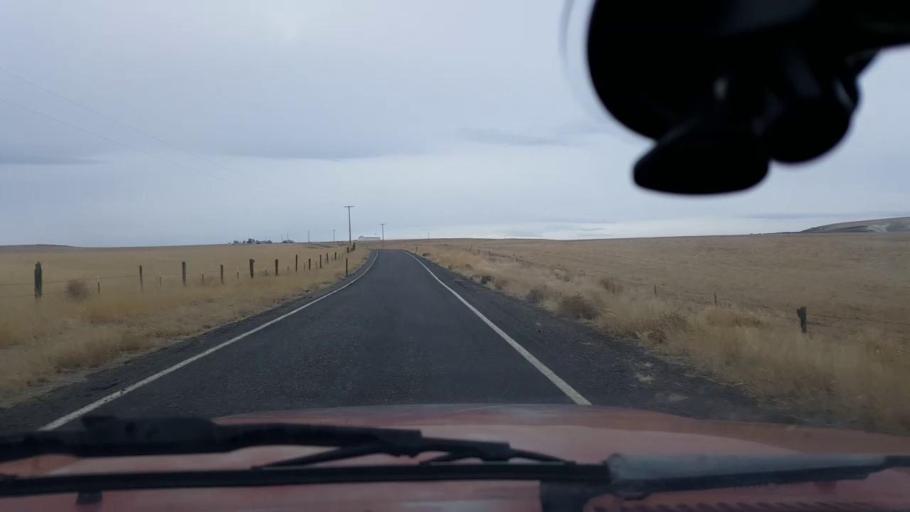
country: US
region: Washington
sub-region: Asotin County
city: Clarkston Heights-Vineland
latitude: 46.3285
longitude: -117.3227
